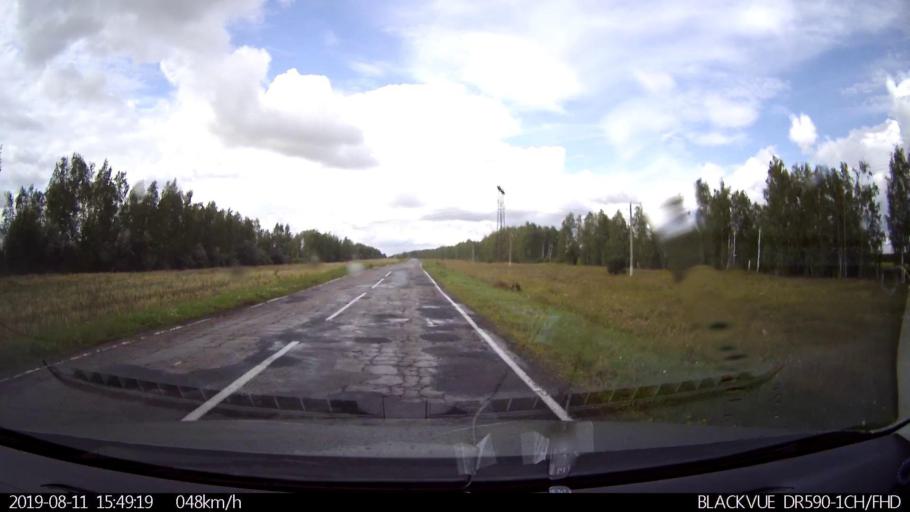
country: RU
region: Ulyanovsk
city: Ignatovka
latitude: 53.9034
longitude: 47.6549
